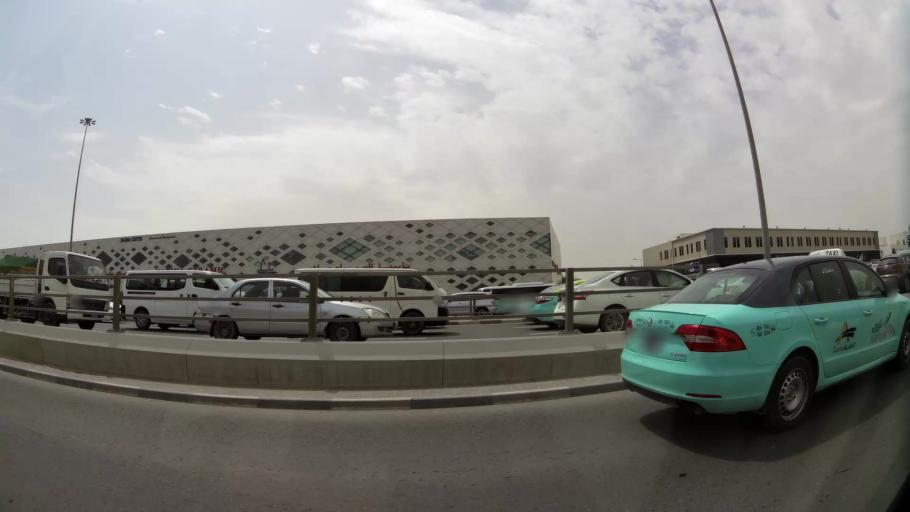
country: QA
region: Baladiyat ar Rayyan
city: Ar Rayyan
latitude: 25.3242
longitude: 51.4684
